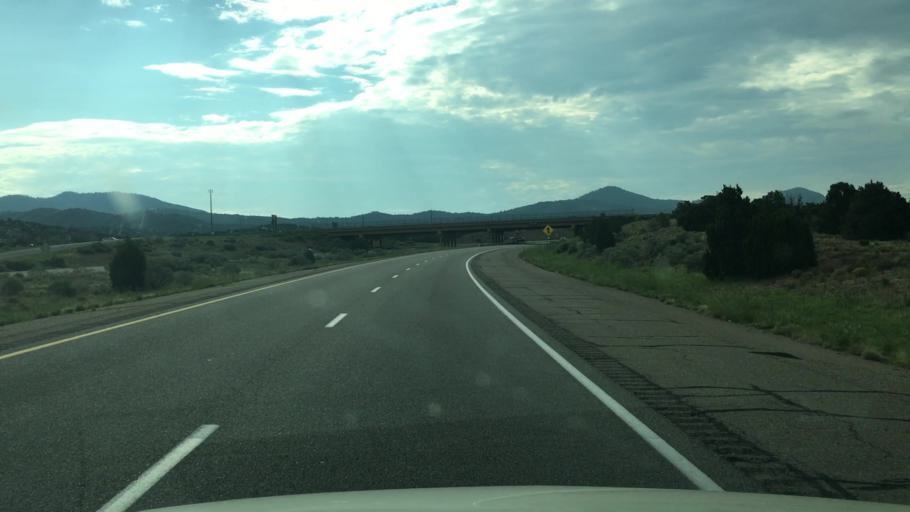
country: US
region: New Mexico
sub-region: Santa Fe County
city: Santa Fe
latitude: 35.6373
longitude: -105.9338
